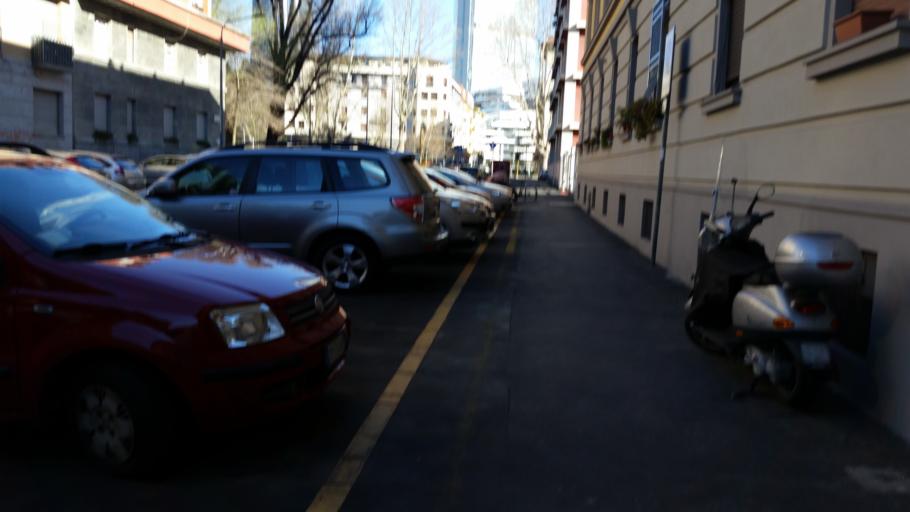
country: IT
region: Lombardy
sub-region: Citta metropolitana di Milano
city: Milano
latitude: 45.4726
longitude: 9.1571
